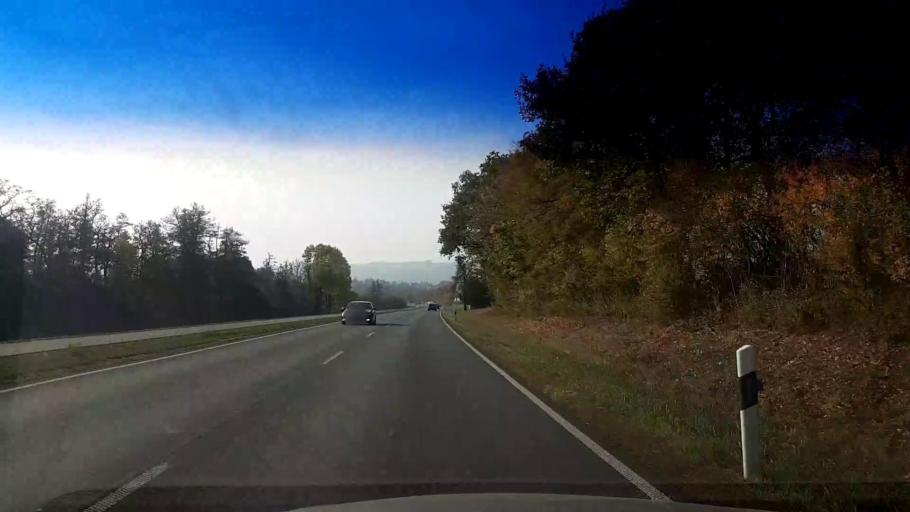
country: DE
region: Bavaria
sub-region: Upper Franconia
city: Himmelkron
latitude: 50.0716
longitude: 11.6081
